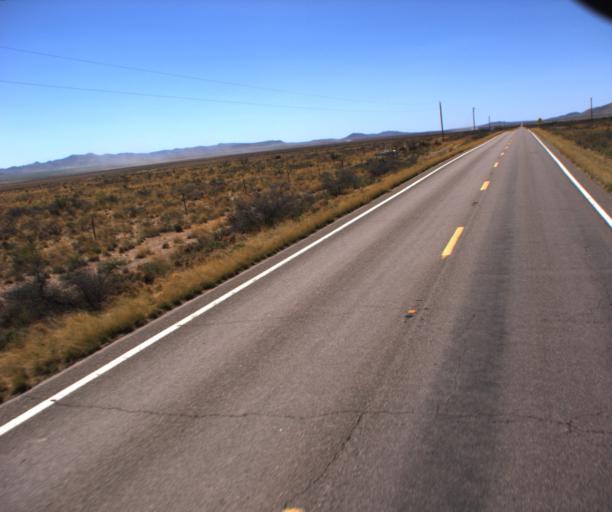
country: US
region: Arizona
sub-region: Cochise County
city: Douglas
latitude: 31.7579
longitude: -109.0860
